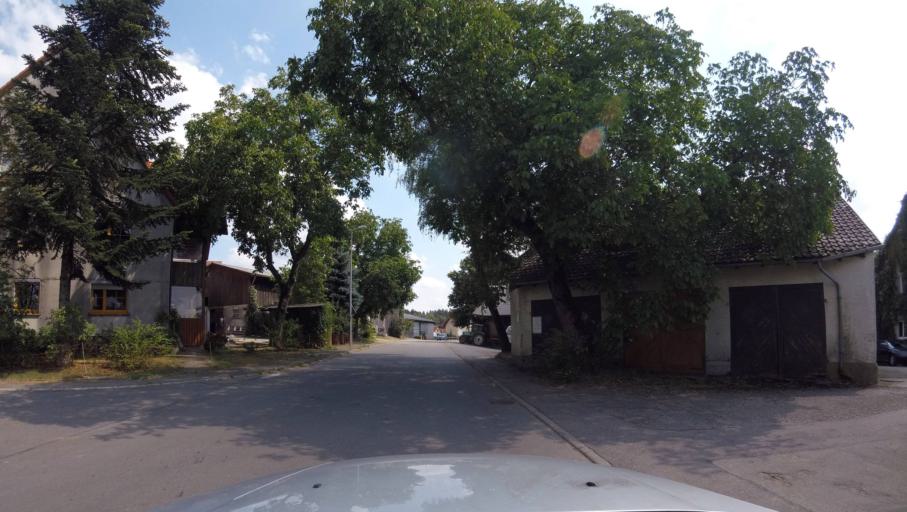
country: DE
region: Baden-Wuerttemberg
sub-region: Regierungsbezirk Stuttgart
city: Welzheim
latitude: 48.8782
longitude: 9.6760
